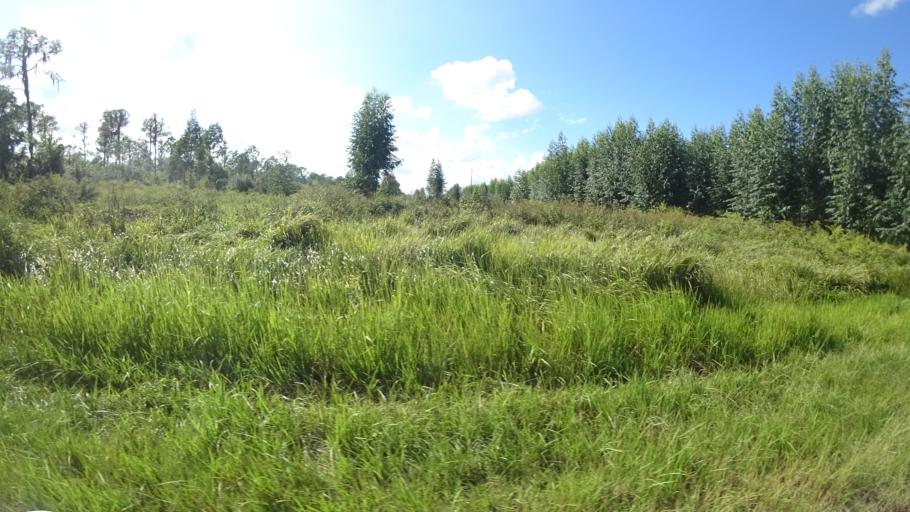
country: US
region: Florida
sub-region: Hardee County
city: Wauchula
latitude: 27.4707
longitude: -82.0554
